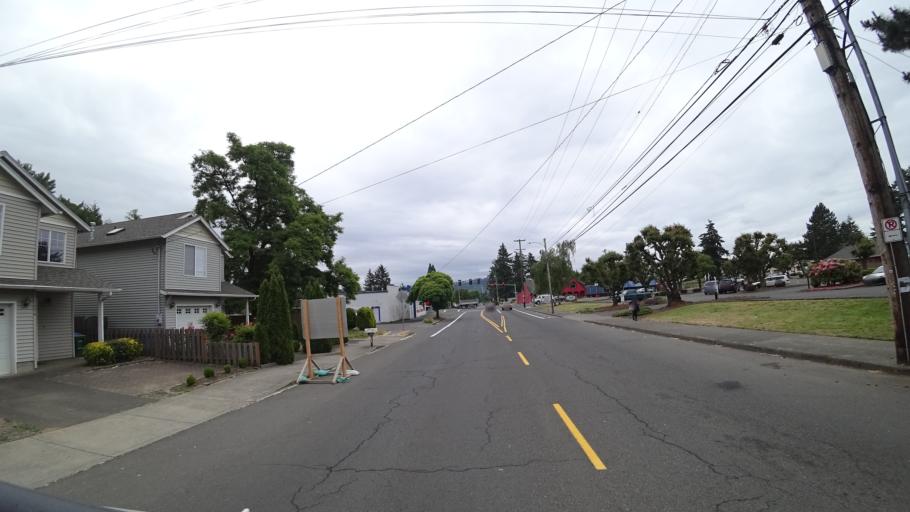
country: US
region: Oregon
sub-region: Multnomah County
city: Lents
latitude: 45.4974
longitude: -122.5480
